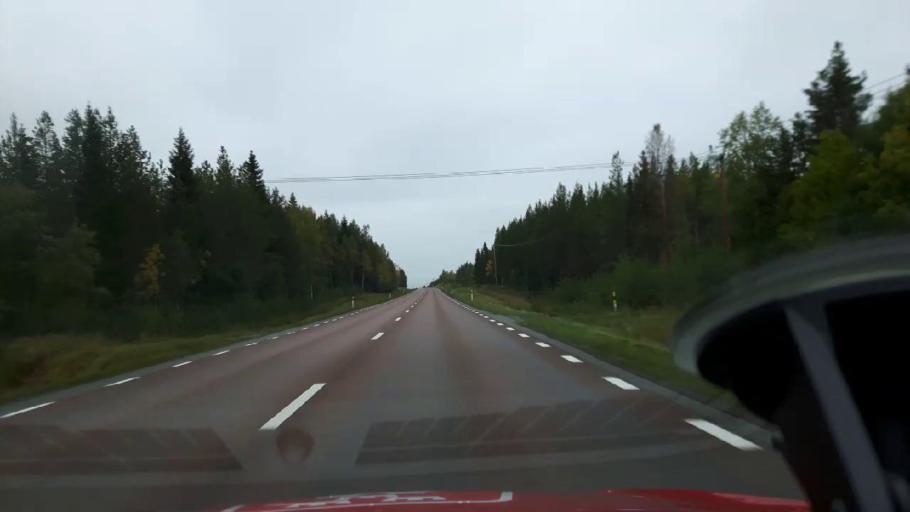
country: SE
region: Jaemtland
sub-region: Bergs Kommun
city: Hoverberg
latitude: 62.8559
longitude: 14.5179
